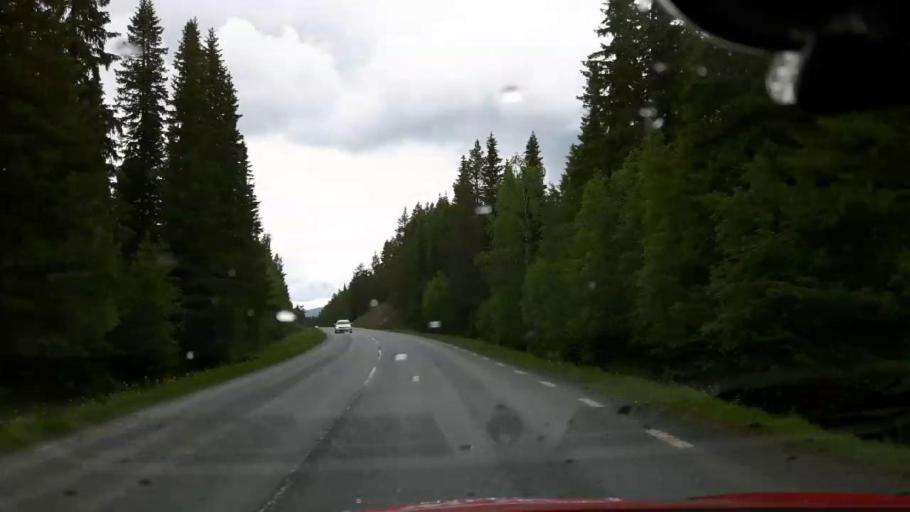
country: SE
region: Jaemtland
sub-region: Krokoms Kommun
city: Krokom
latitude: 63.4143
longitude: 14.2363
